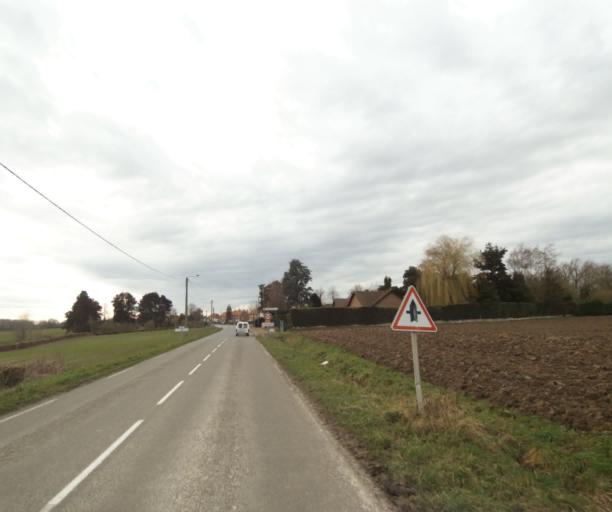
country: FR
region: Nord-Pas-de-Calais
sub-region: Departement du Nord
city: Sebourg
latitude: 50.3532
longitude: 3.6392
